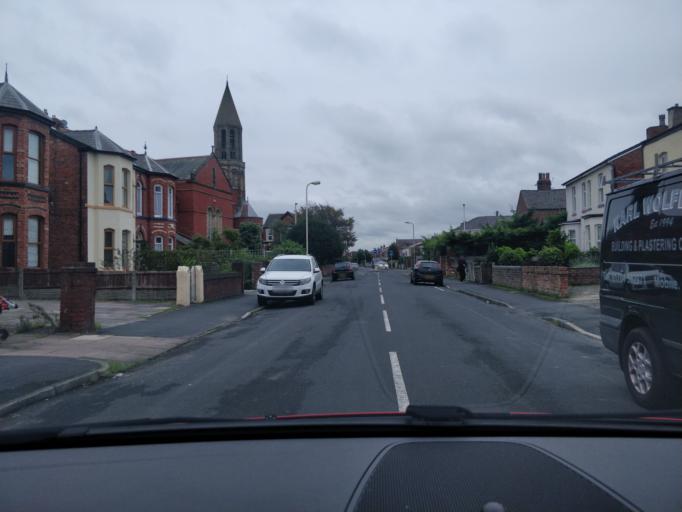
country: GB
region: England
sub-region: Sefton
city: Southport
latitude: 53.6390
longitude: -2.9959
